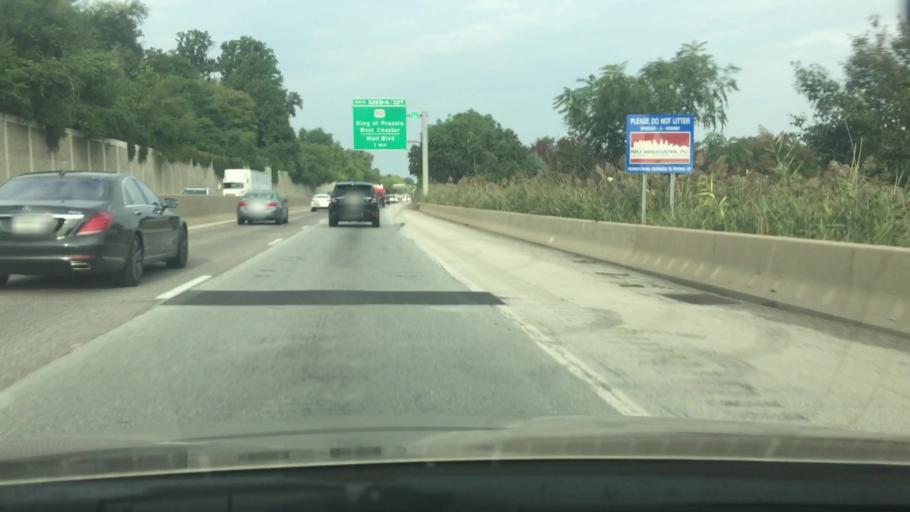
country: US
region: Pennsylvania
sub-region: Delaware County
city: Radnor
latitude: 40.0765
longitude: -75.3656
